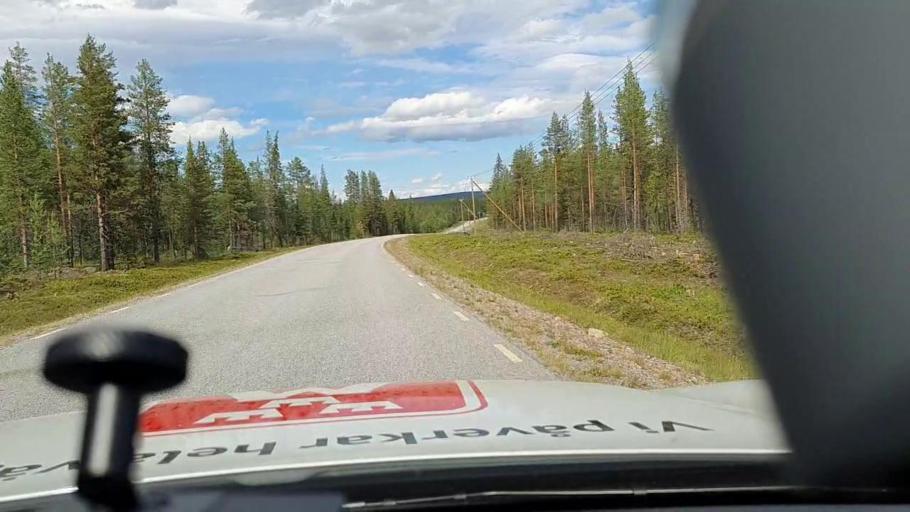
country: SE
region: Norrbotten
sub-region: Jokkmokks Kommun
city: Jokkmokk
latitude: 66.6859
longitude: 20.1669
